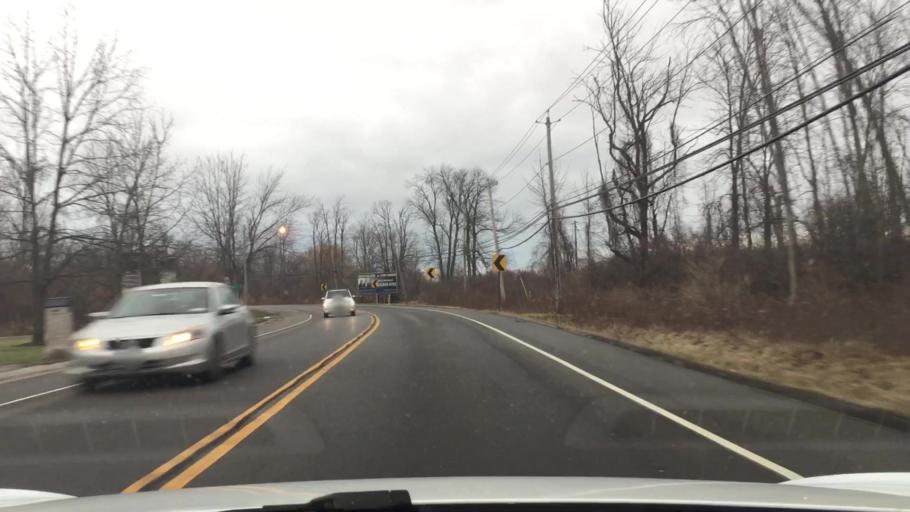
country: US
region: New York
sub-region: Erie County
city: Tonawanda
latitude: 43.0633
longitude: -78.9161
